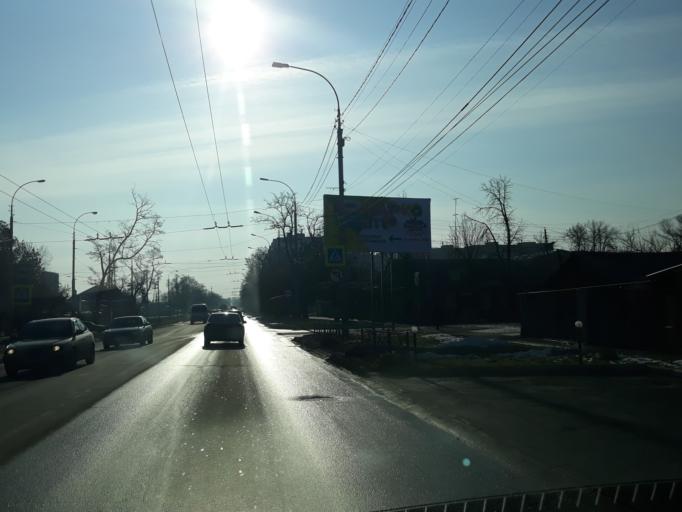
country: RU
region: Rostov
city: Taganrog
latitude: 47.2309
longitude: 38.9050
